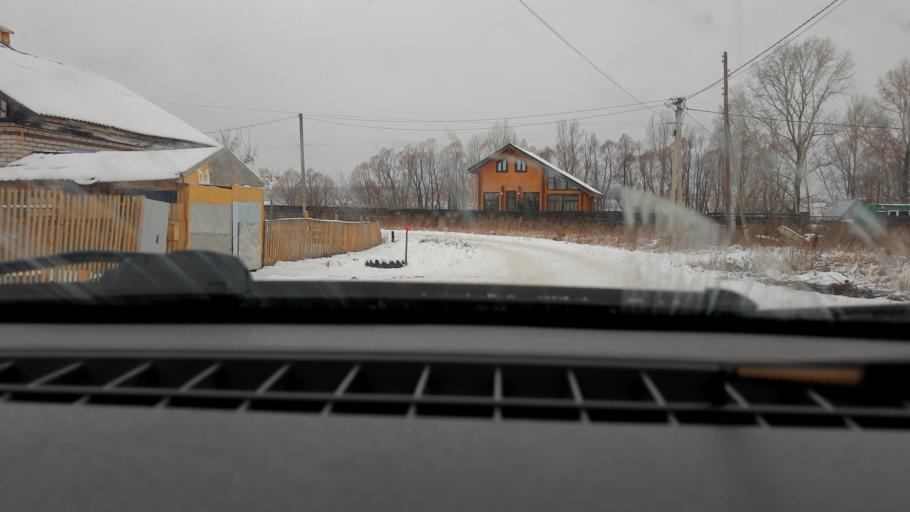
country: RU
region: Bashkortostan
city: Kabakovo
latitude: 54.6988
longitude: 56.2413
